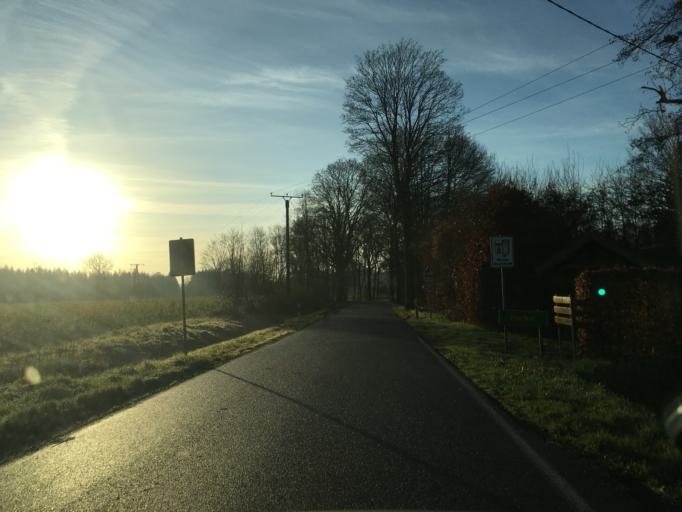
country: DE
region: North Rhine-Westphalia
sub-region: Regierungsbezirk Munster
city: Horstmar
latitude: 52.0579
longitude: 7.2671
